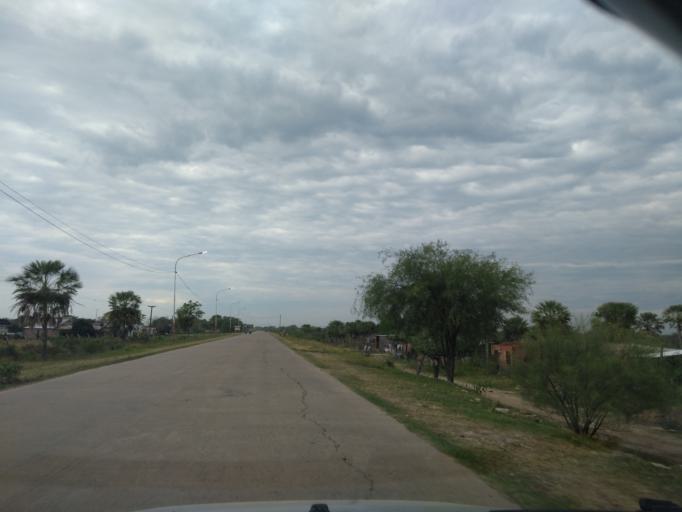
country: AR
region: Chaco
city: Puerto Vilelas
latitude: -27.5317
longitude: -58.9285
